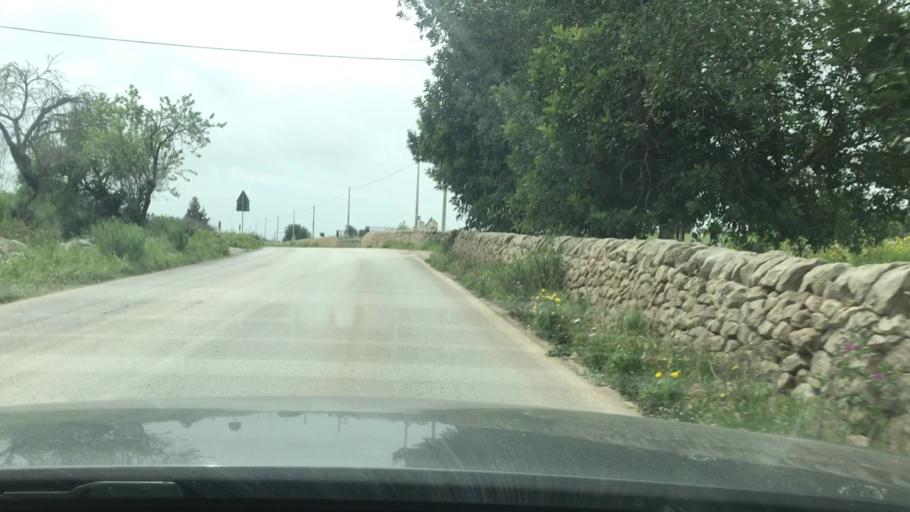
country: IT
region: Sicily
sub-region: Ragusa
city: Scicli
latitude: 36.8089
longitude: 14.7264
